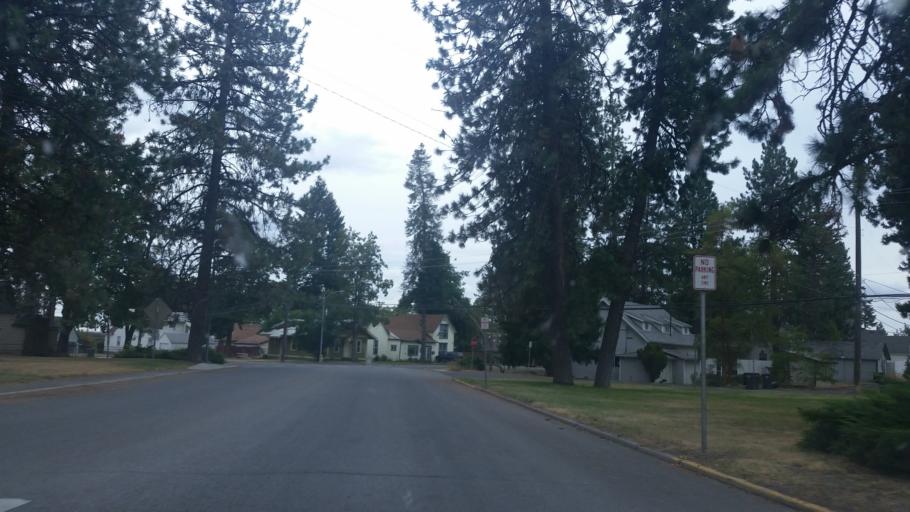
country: US
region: Washington
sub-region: Spokane County
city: Cheney
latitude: 47.4927
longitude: -117.5756
